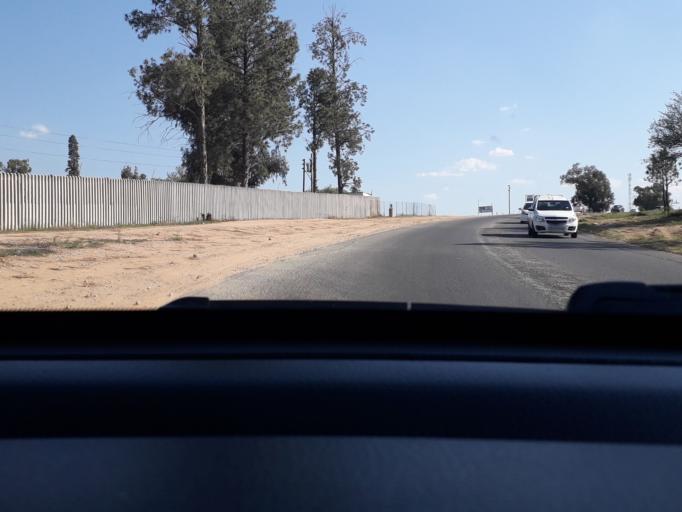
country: ZA
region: Gauteng
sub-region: City of Johannesburg Metropolitan Municipality
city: Midrand
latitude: -26.0335
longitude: 28.1113
